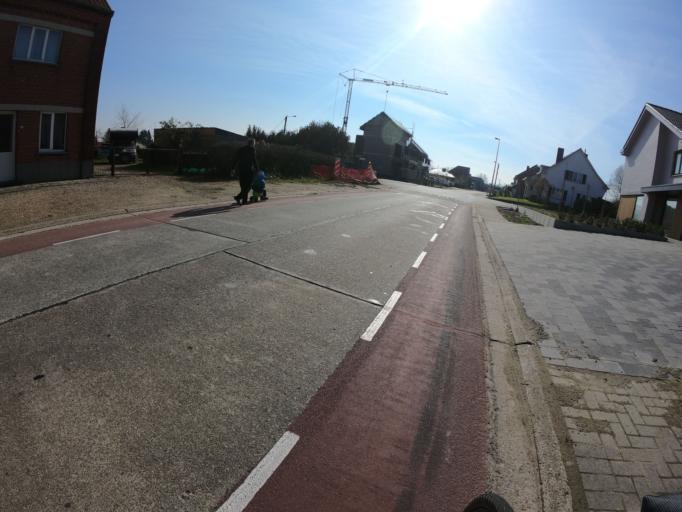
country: BE
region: Flanders
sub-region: Provincie Limburg
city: Lummen
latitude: 50.9601
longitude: 5.1901
